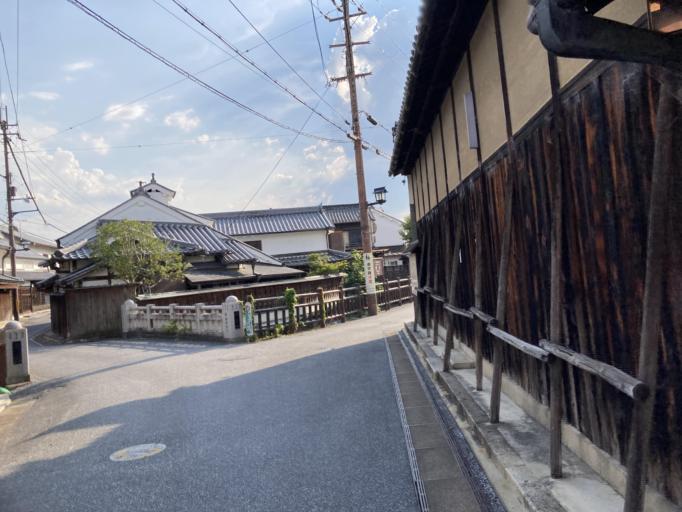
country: JP
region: Nara
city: Gojo
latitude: 34.3500
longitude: 135.6950
